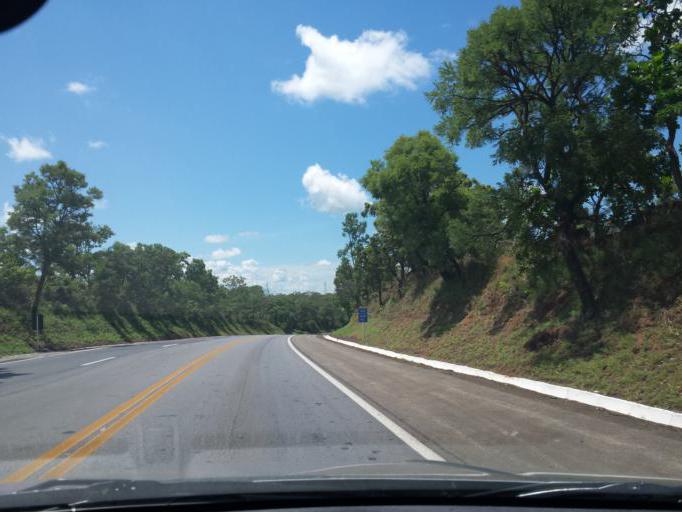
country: BR
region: Goias
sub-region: Luziania
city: Luziania
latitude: -16.3673
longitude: -47.8271
